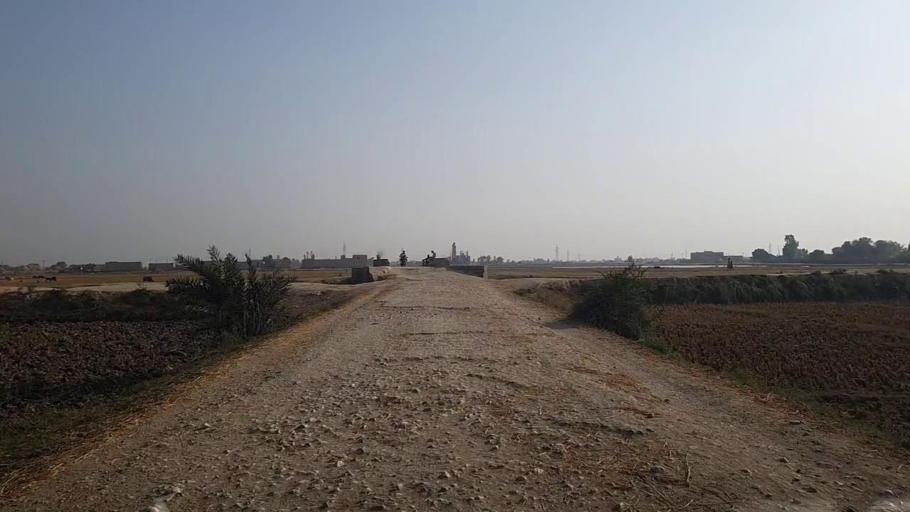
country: PK
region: Sindh
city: Kandhkot
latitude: 28.2808
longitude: 69.2563
